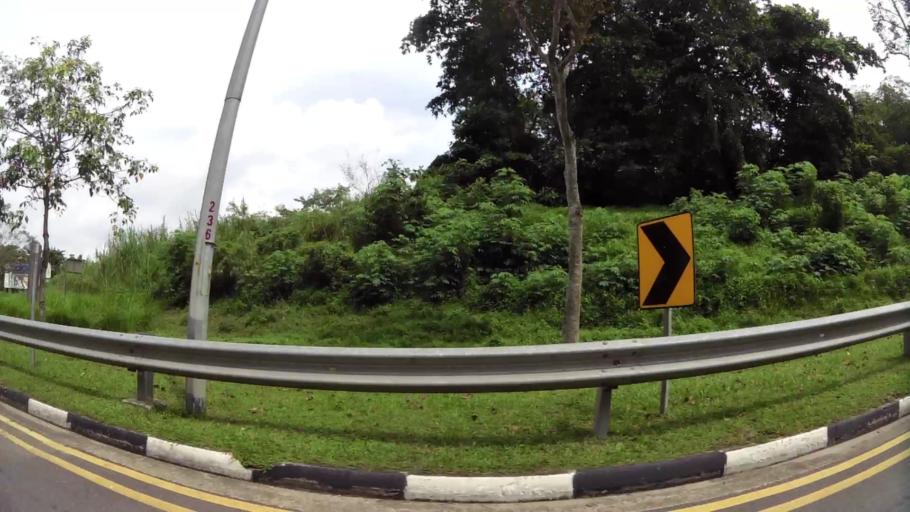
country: MY
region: Johor
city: Kampung Pasir Gudang Baru
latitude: 1.3837
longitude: 103.9369
